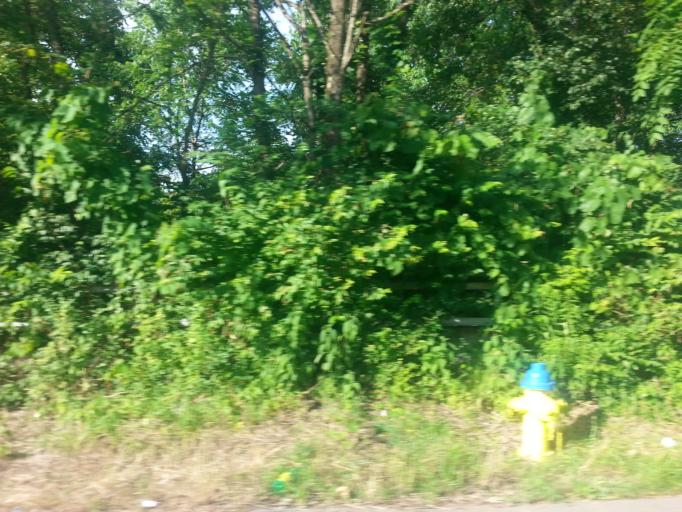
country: US
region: Tennessee
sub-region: Knox County
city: Knoxville
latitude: 35.9262
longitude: -83.9211
